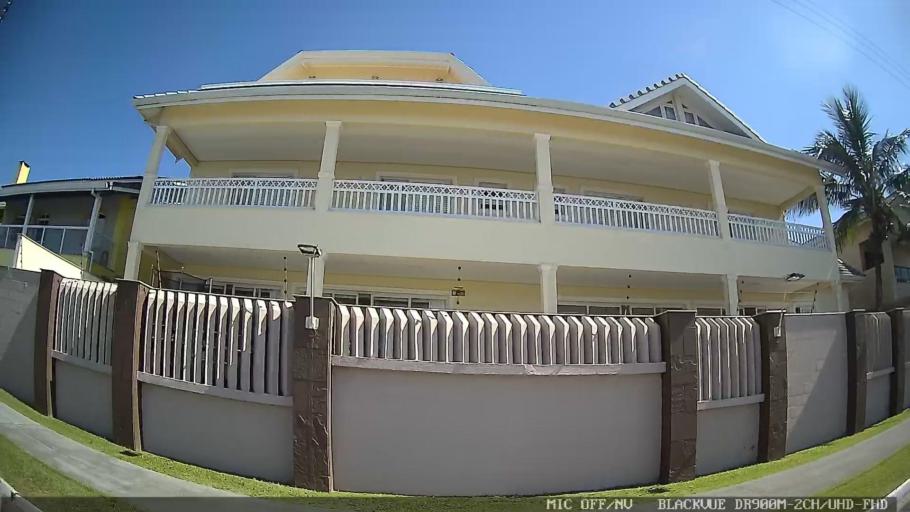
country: BR
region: Sao Paulo
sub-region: Peruibe
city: Peruibe
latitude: -24.2858
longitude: -46.9500
